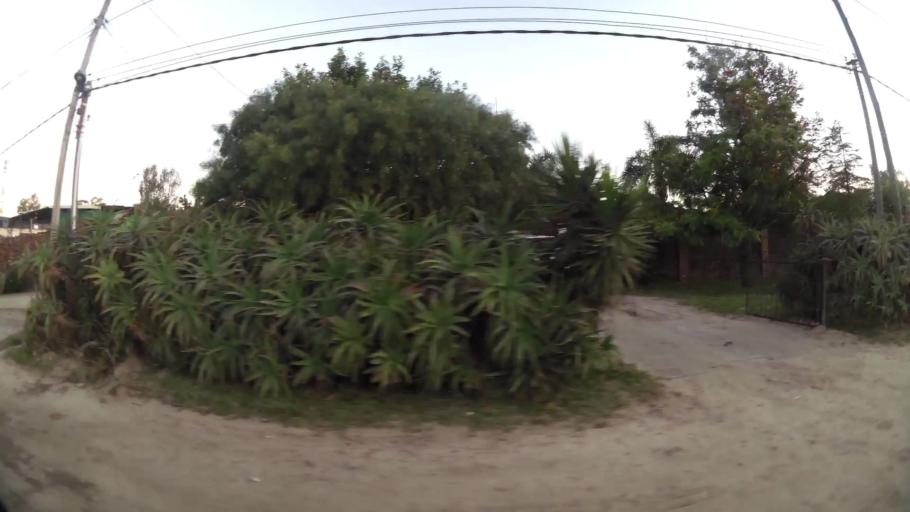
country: UY
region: Canelones
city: Colonia Nicolich
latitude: -34.8239
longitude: -55.9615
